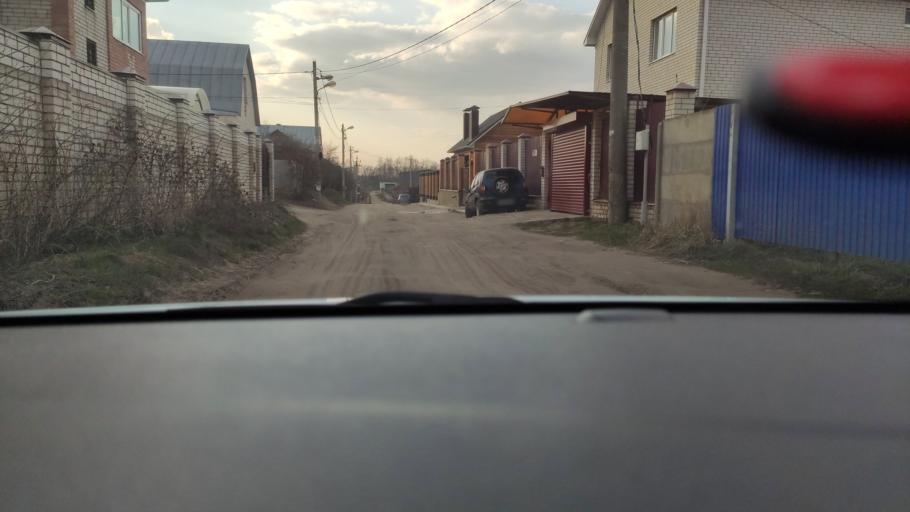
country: RU
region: Voronezj
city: Pridonskoy
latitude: 51.6369
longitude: 39.0948
